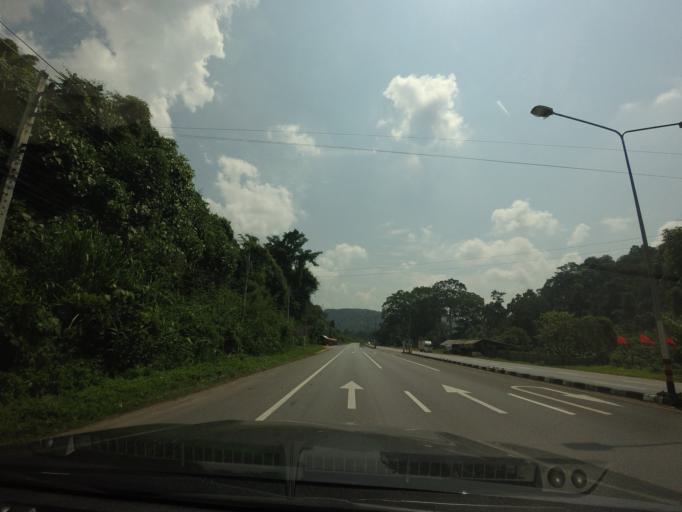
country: TH
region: Uttaradit
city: Lap Lae
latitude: 17.8044
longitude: 100.1112
